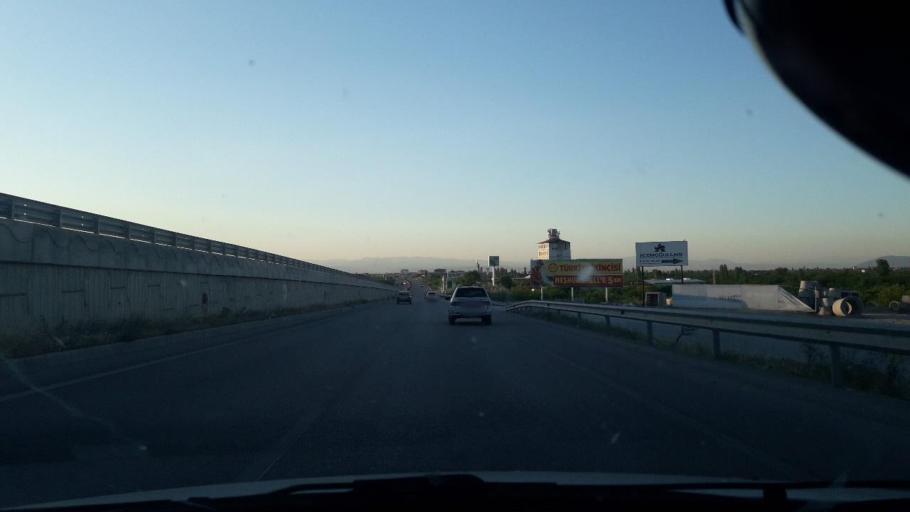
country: TR
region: Malatya
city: Yesilyurt
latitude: 38.3415
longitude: 38.2343
